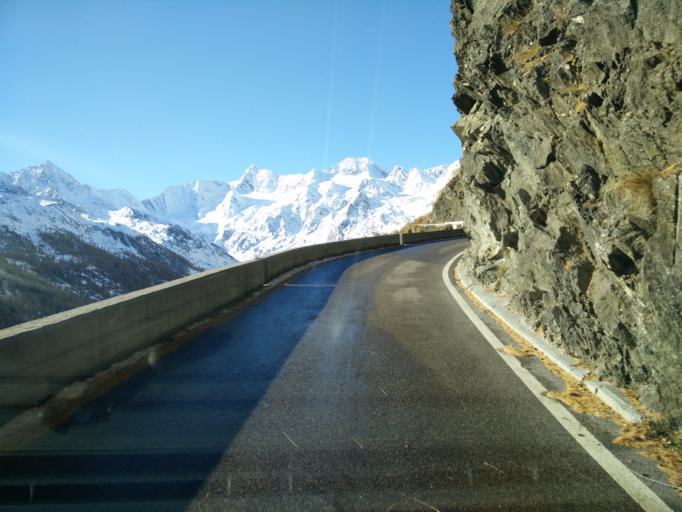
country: IT
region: Trentino-Alto Adige
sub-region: Bolzano
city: Moso in Passiria
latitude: 46.8837
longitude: 11.1179
